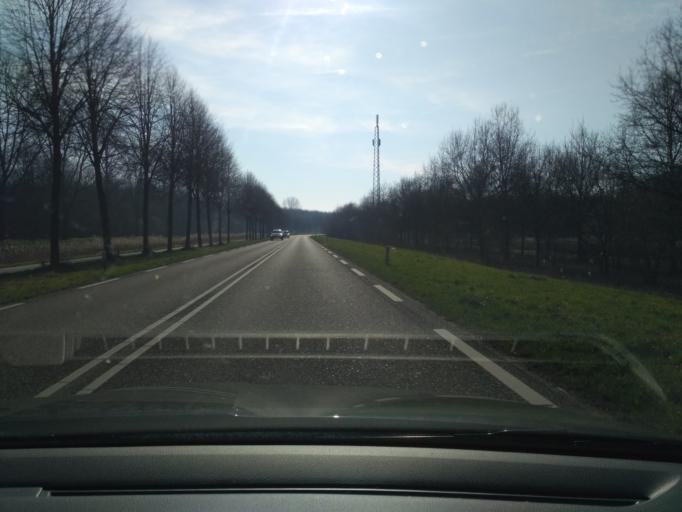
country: NL
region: Flevoland
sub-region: Gemeente Zeewolde
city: Zeewolde
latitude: 52.3206
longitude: 5.5188
